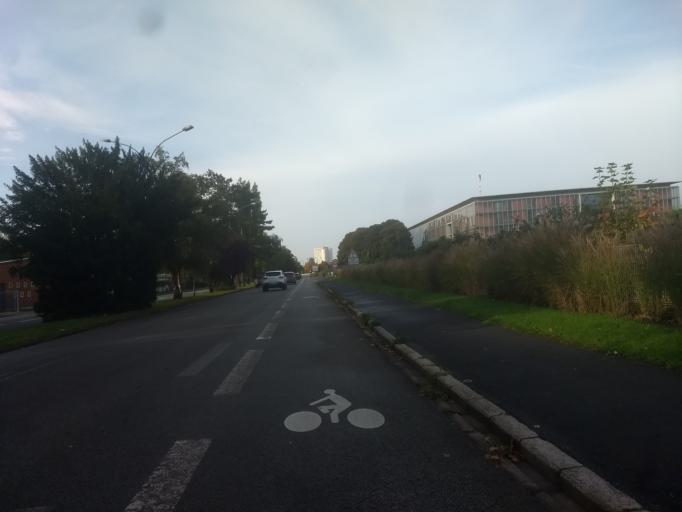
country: FR
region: Nord-Pas-de-Calais
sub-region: Departement du Pas-de-Calais
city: Sainte-Catherine
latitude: 50.2965
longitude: 2.7617
